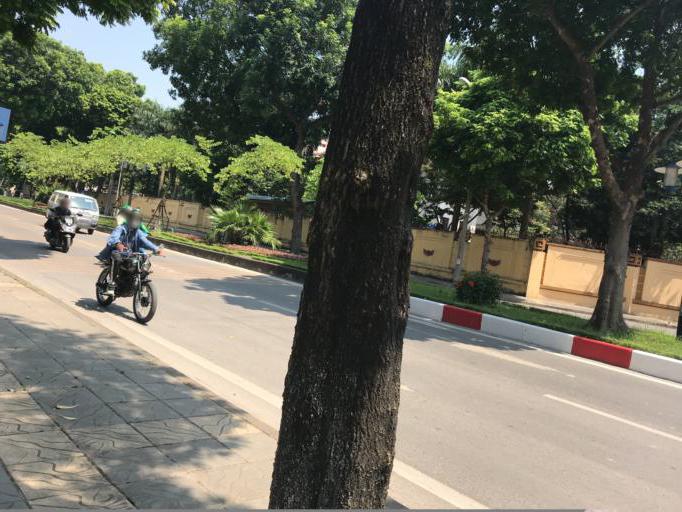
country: VN
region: Ha Noi
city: Hanoi
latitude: 21.0357
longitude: 105.8410
